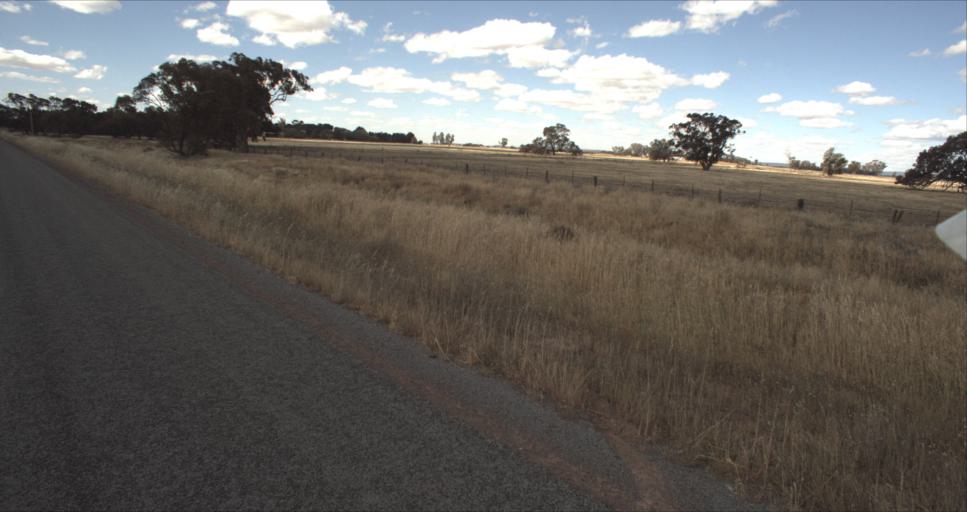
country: AU
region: New South Wales
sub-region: Leeton
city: Leeton
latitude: -34.4890
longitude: 146.2476
